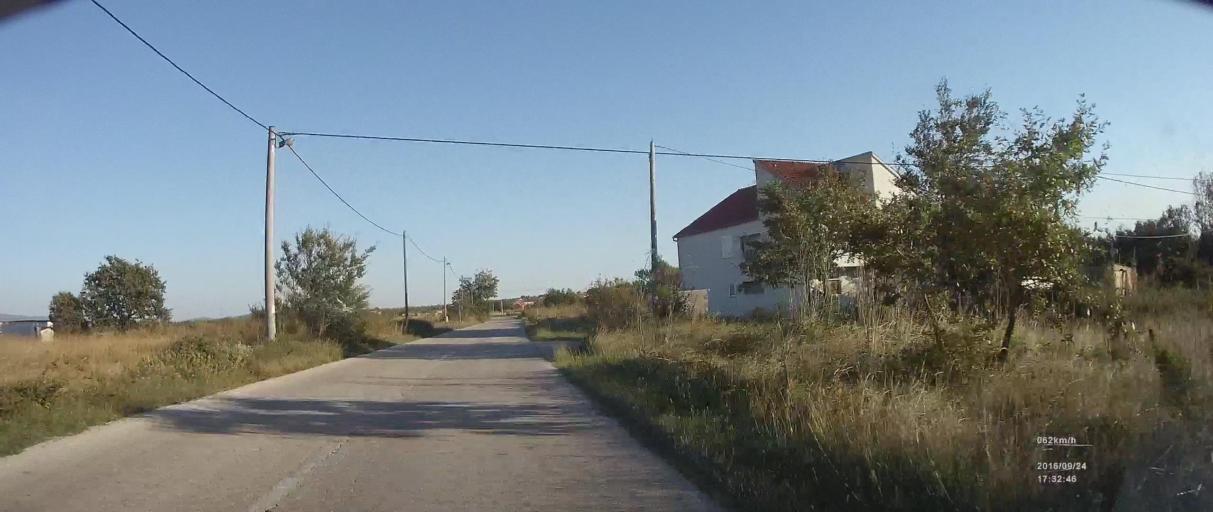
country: HR
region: Zadarska
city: Posedarje
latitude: 44.1798
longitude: 15.4528
